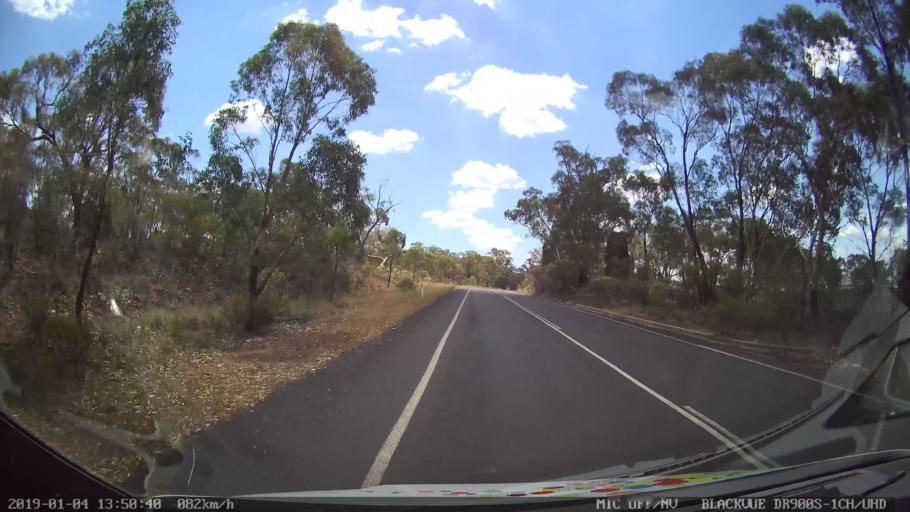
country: AU
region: New South Wales
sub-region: Dubbo Municipality
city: Dubbo
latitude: -32.4170
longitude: 148.5714
